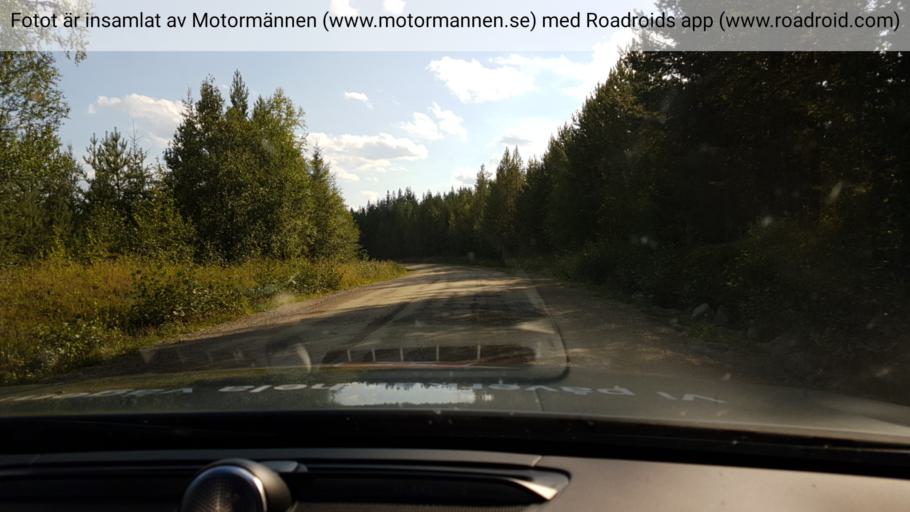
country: SE
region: Vaesternorrland
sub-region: Solleftea Kommun
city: As
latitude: 63.7933
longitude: 16.3941
